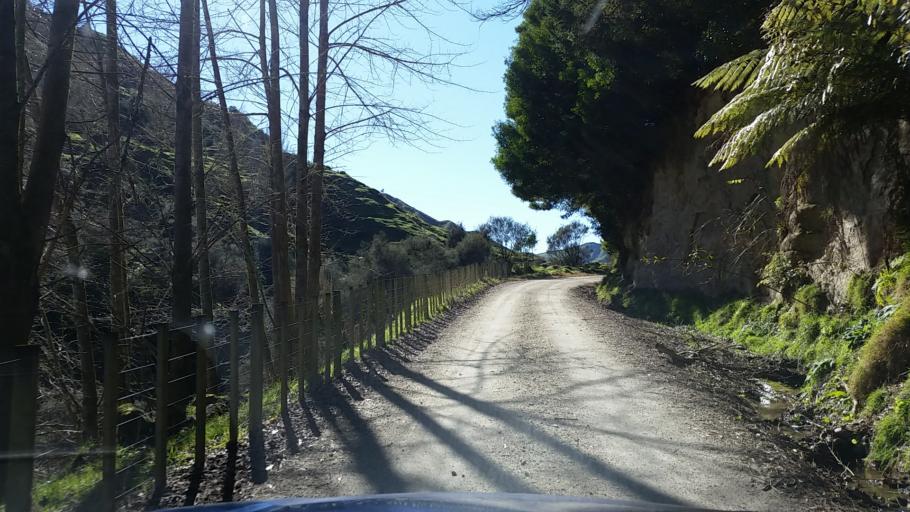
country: NZ
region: Manawatu-Wanganui
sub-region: Wanganui District
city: Wanganui
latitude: -39.5403
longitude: 174.9122
